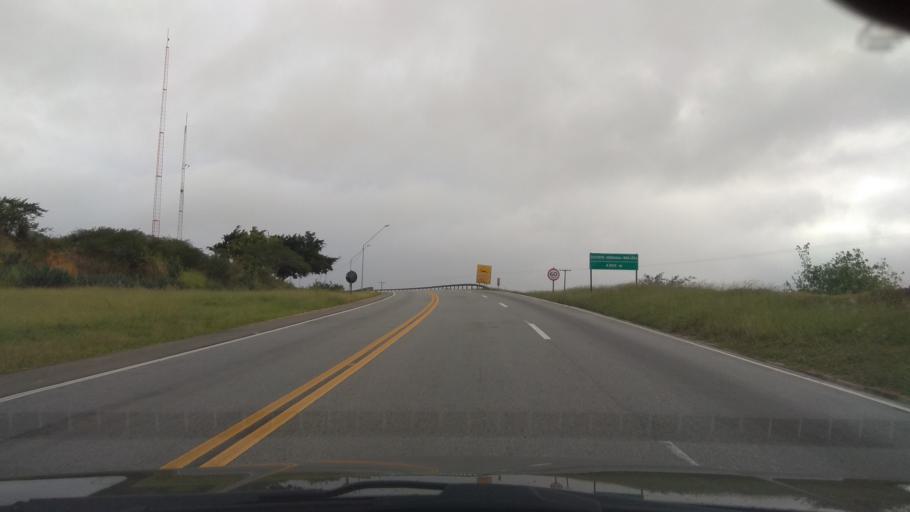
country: BR
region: Bahia
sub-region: Santa Ines
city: Santa Ines
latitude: -13.0657
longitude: -39.9595
